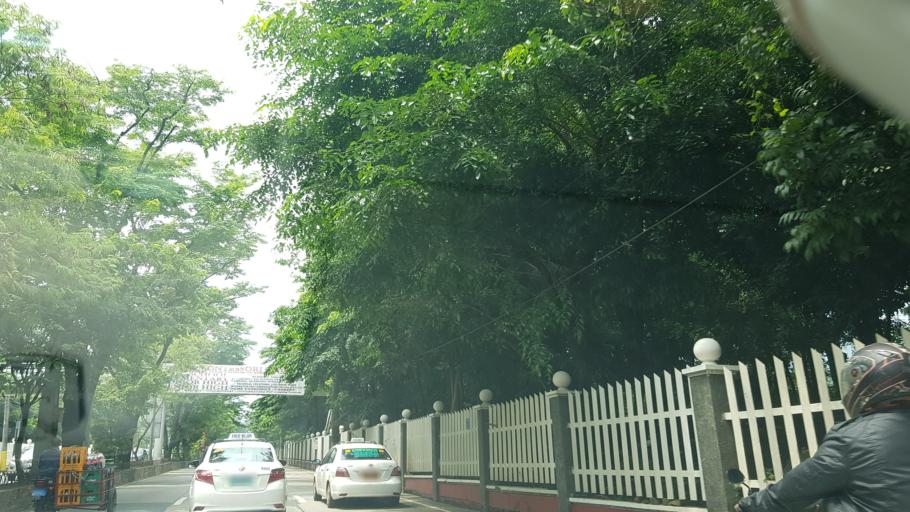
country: PH
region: Metro Manila
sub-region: Makati City
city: Makati City
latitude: 14.5324
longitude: 121.0411
